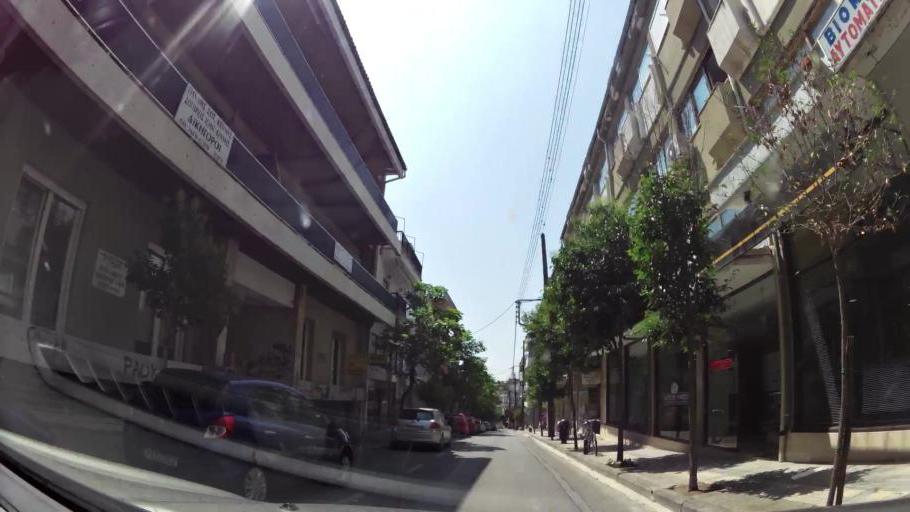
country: GR
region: West Macedonia
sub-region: Nomos Kozanis
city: Kozani
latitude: 40.3037
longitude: 21.7847
